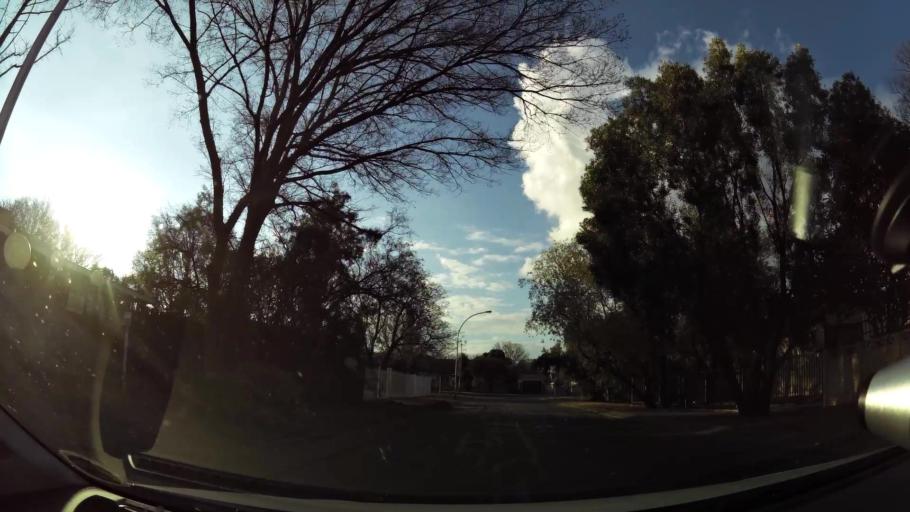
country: ZA
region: Orange Free State
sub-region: Mangaung Metropolitan Municipality
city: Bloemfontein
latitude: -29.1465
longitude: 26.1808
